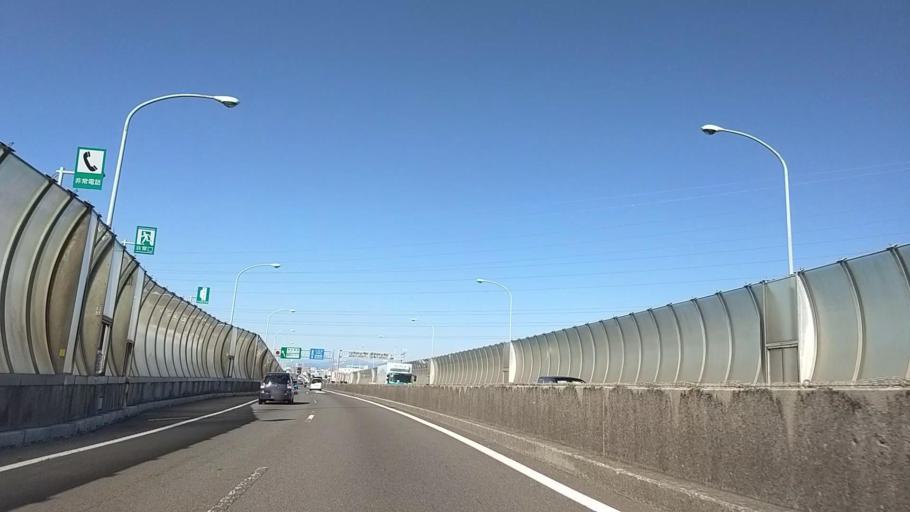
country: JP
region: Kanagawa
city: Minami-rinkan
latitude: 35.5023
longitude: 139.4897
